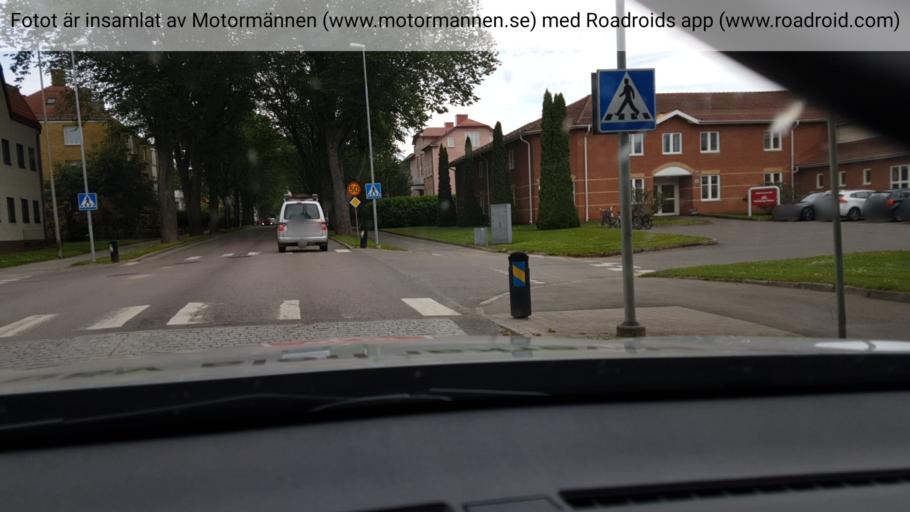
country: SE
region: Vaestra Goetaland
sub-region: Falkopings Kommun
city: Falkoeping
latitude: 58.1659
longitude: 13.5478
